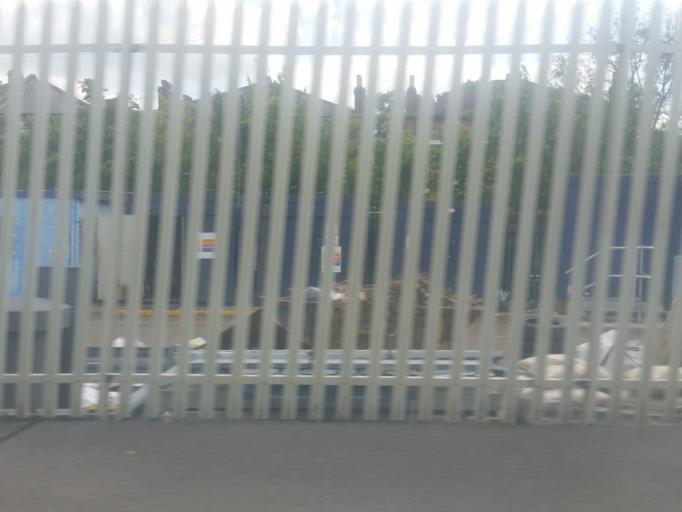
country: GB
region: England
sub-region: Greater London
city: Brixton Hill
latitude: 51.4394
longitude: -0.1052
